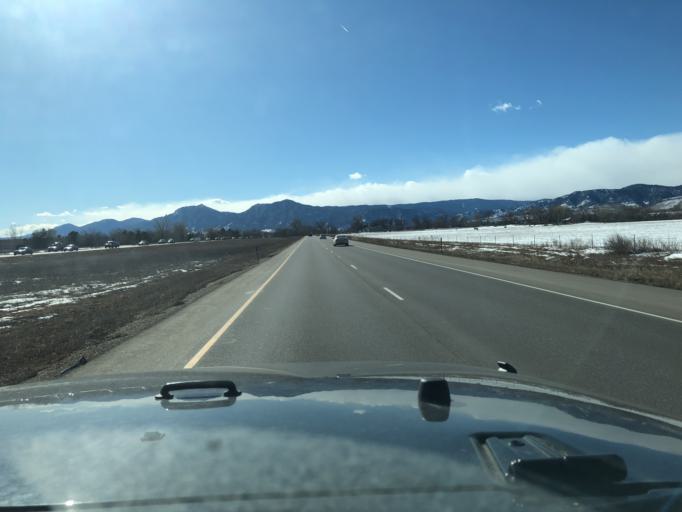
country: US
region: Colorado
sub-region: Boulder County
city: Gunbarrel
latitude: 40.0640
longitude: -105.2183
